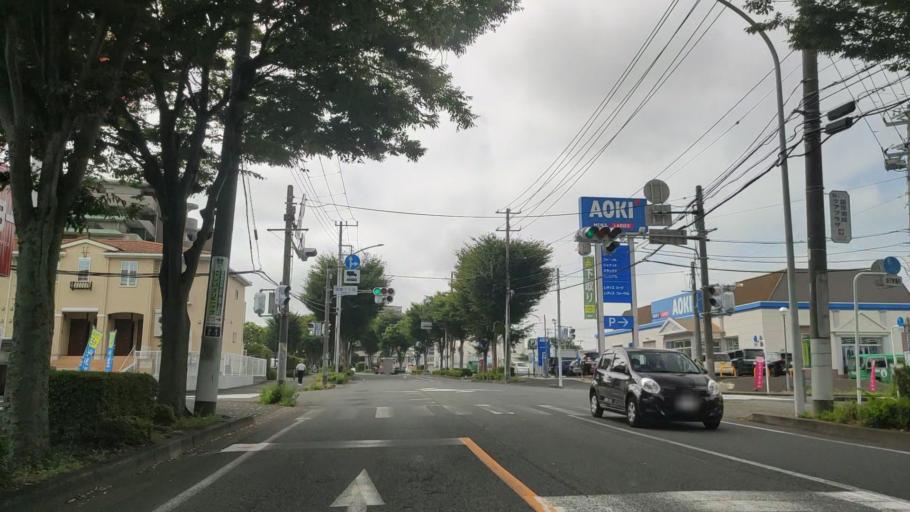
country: JP
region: Kanagawa
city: Fujisawa
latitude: 35.4205
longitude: 139.5245
